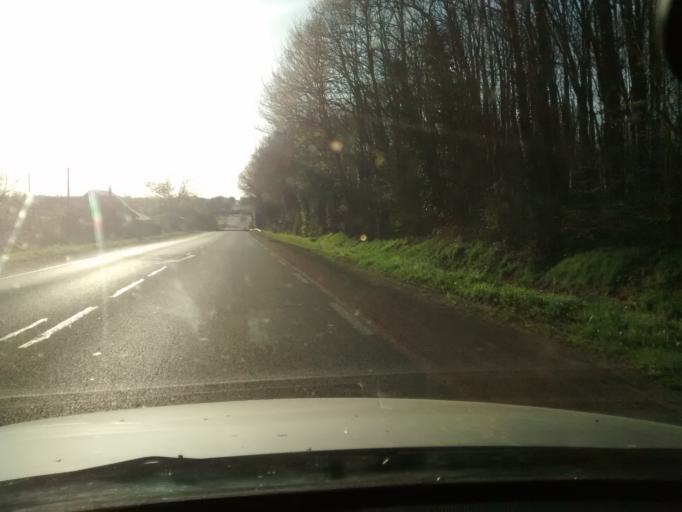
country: FR
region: Pays de la Loire
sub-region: Departement de la Sarthe
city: Rouillon
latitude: 48.0183
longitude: 0.1316
